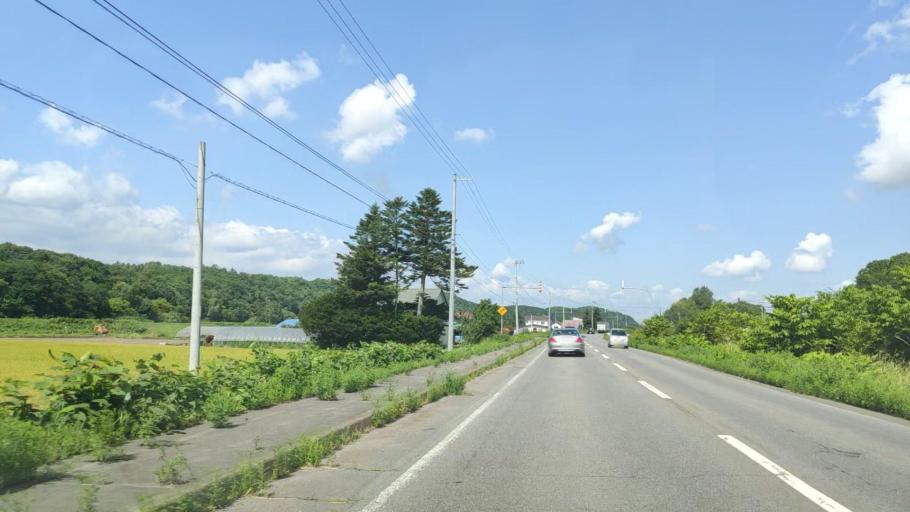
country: JP
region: Hokkaido
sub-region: Asahikawa-shi
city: Asahikawa
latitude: 43.6310
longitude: 142.4604
